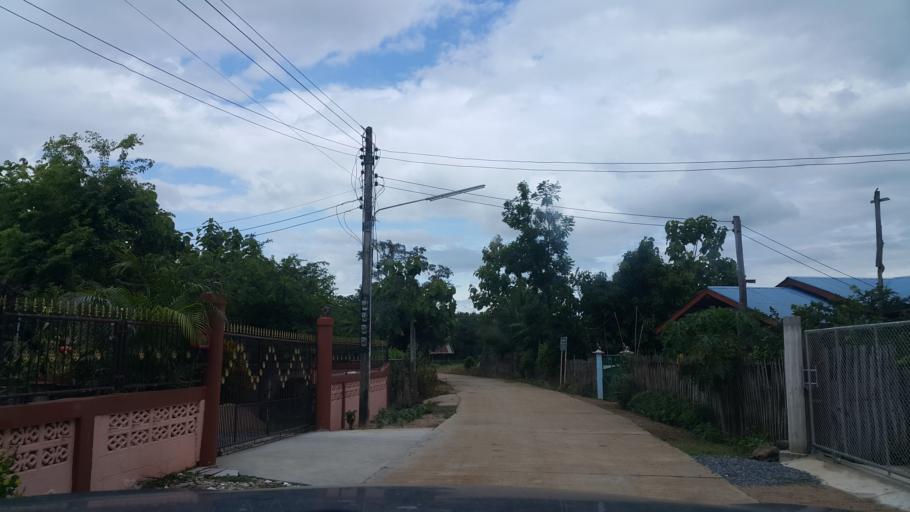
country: TH
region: Sukhothai
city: Thung Saliam
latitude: 17.3188
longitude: 99.5799
